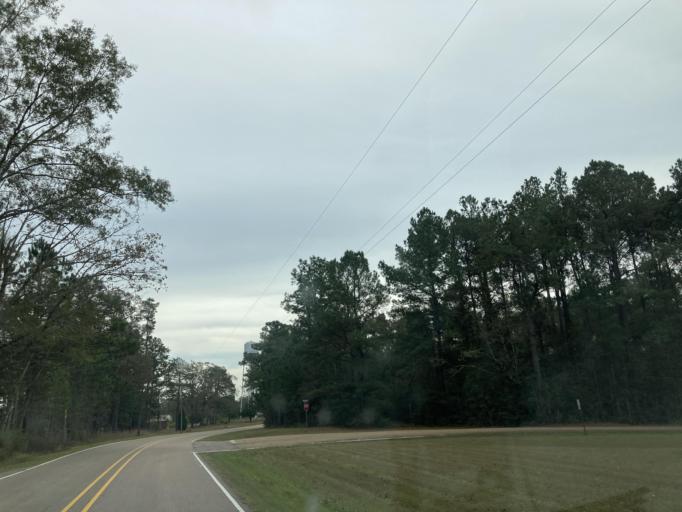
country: US
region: Mississippi
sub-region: Lamar County
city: Lumberton
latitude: 31.0559
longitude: -89.4764
